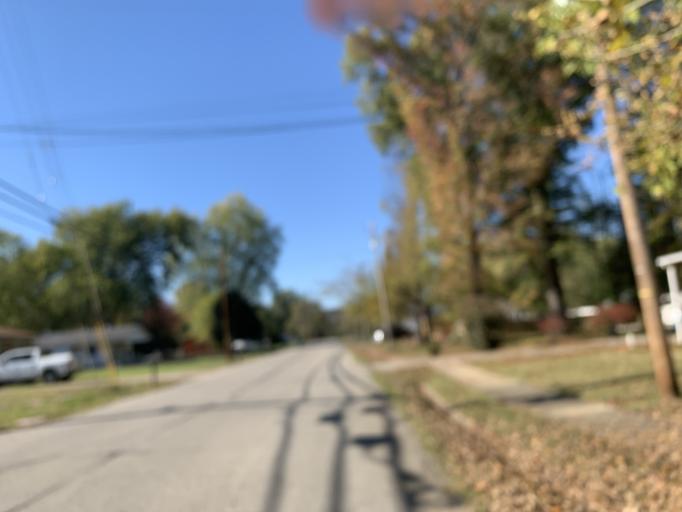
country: US
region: Kentucky
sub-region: Jefferson County
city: Saint Dennis
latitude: 38.1923
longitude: -85.8731
